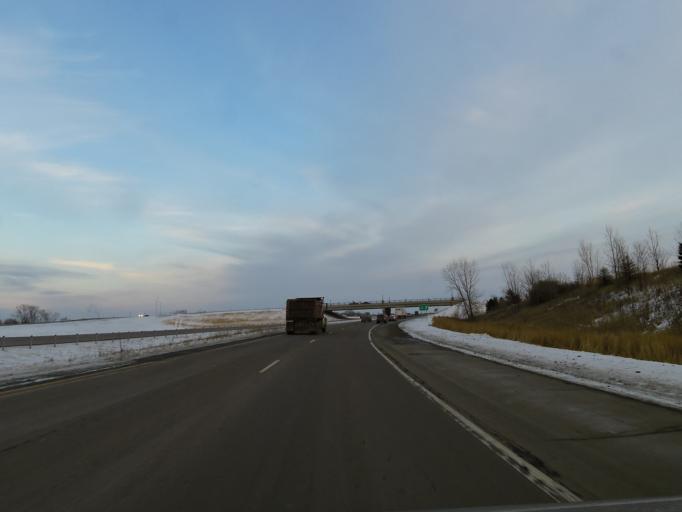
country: US
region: Minnesota
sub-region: Carver County
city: Chaska
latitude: 44.7775
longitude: -93.5633
